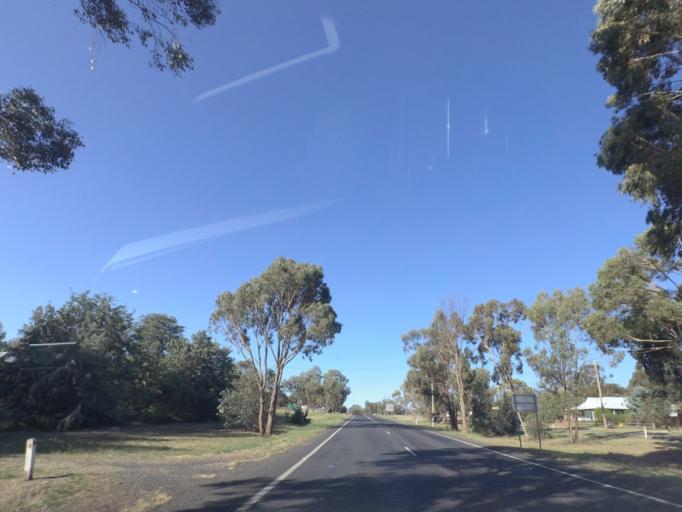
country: AU
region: New South Wales
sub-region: Wagga Wagga
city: Forest Hill
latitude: -35.2728
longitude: 147.7427
